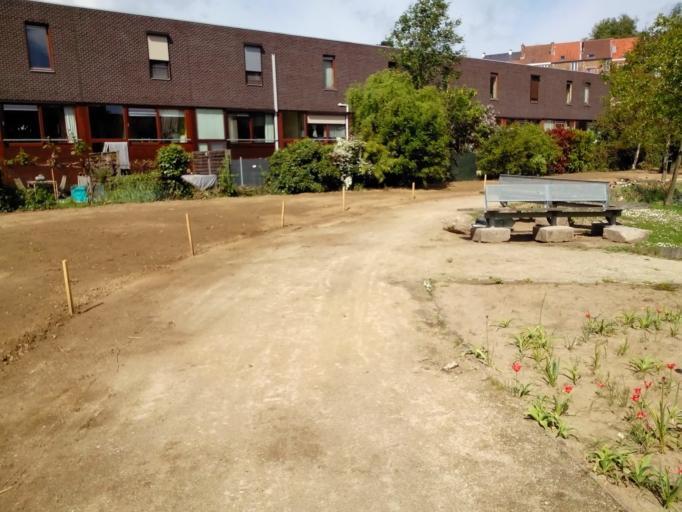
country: BE
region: Flanders
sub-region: Provincie Vlaams-Brabant
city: Leuven
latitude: 50.8854
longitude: 4.6948
